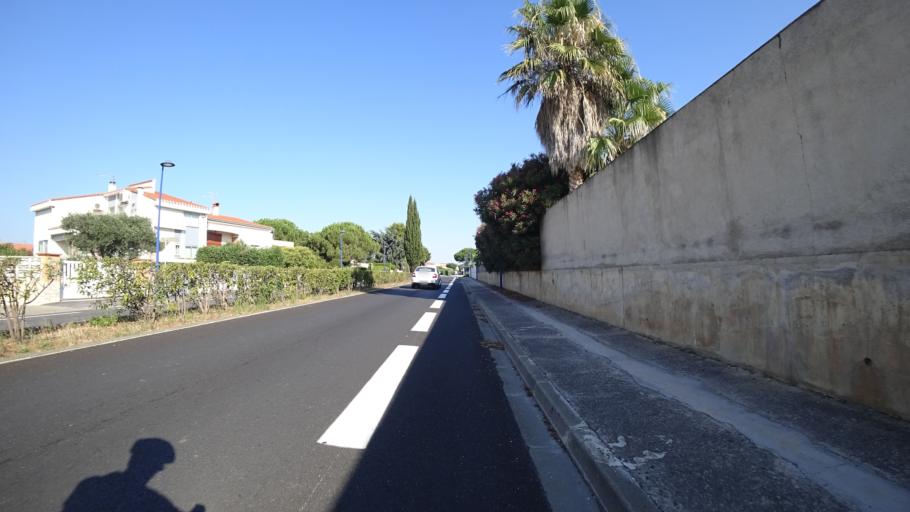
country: FR
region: Languedoc-Roussillon
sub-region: Departement des Pyrenees-Orientales
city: Cabestany
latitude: 42.6834
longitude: 2.9434
